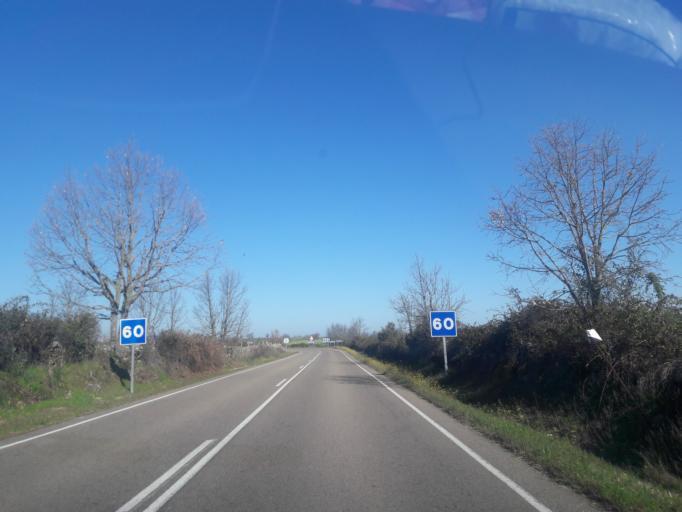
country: ES
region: Castille and Leon
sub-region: Provincia de Salamanca
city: Valderrodrigo
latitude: 41.0686
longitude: -6.5160
